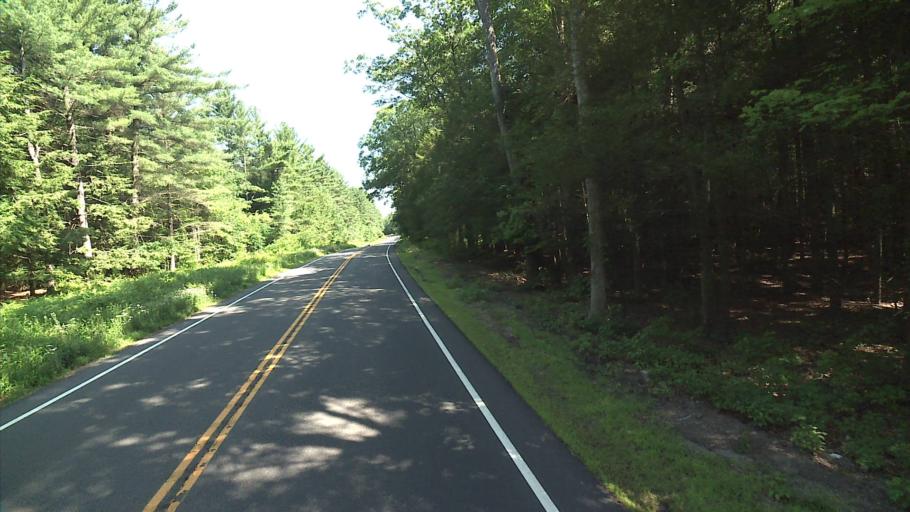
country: US
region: Connecticut
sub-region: Litchfield County
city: Terryville
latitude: 41.7045
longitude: -73.0095
